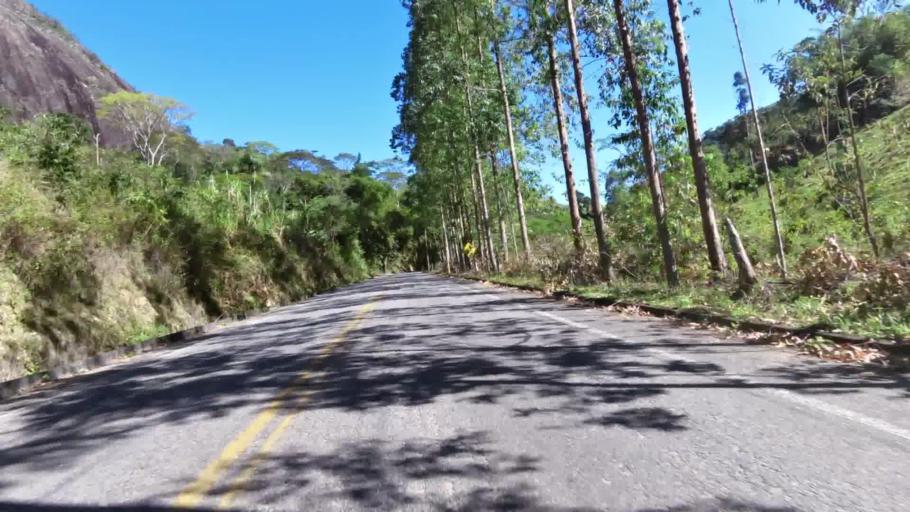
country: BR
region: Espirito Santo
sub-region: Iconha
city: Iconha
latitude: -20.7229
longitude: -40.8937
